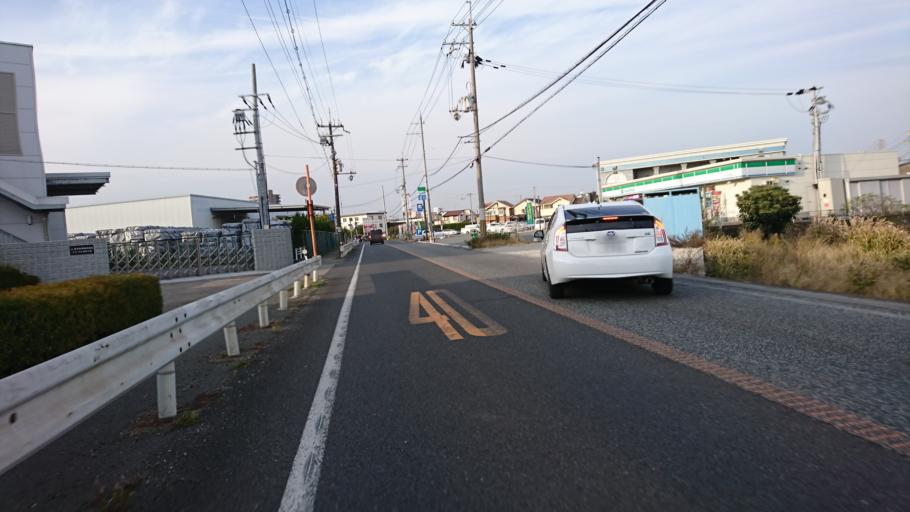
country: JP
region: Hyogo
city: Kakogawacho-honmachi
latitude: 34.7226
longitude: 134.8509
